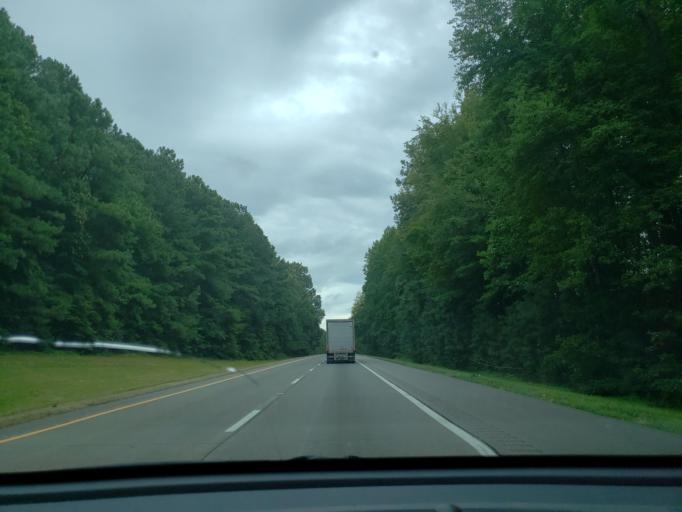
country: US
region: North Carolina
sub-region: Granville County
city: Oxford
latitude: 36.3211
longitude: -78.5174
